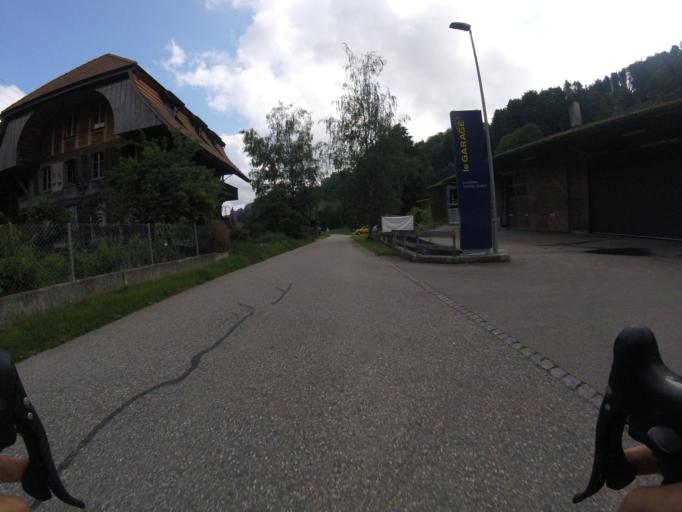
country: CH
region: Bern
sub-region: Emmental District
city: Krauchthal
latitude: 46.9996
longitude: 7.5937
